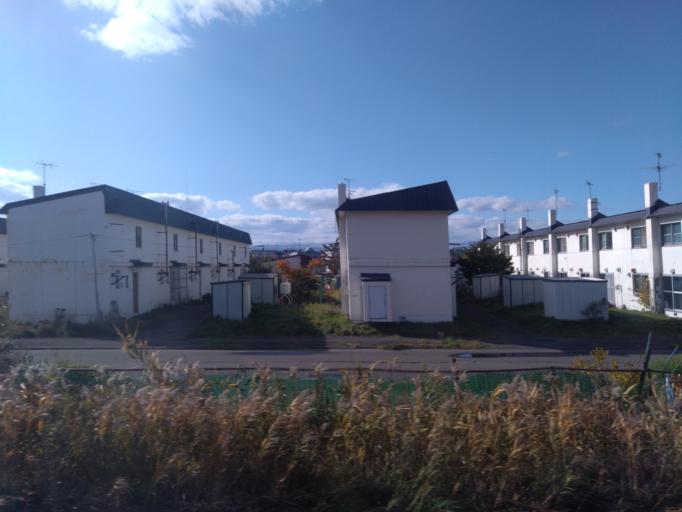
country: JP
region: Hokkaido
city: Kitahiroshima
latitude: 42.8980
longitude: 141.5748
